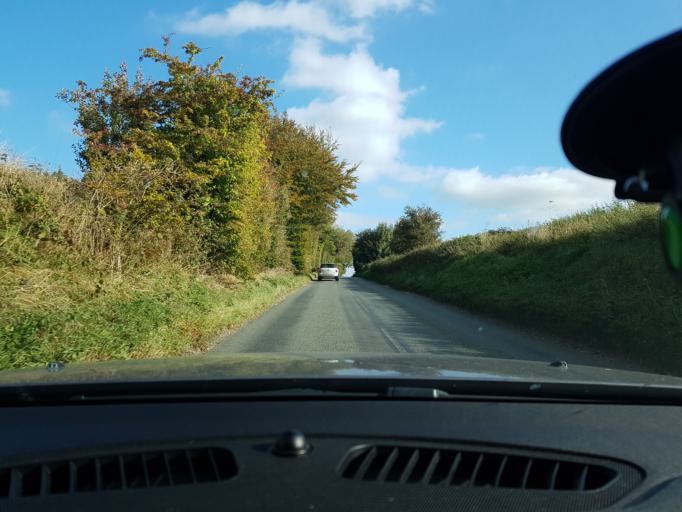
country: GB
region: England
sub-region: Wiltshire
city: Aldbourne
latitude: 51.5091
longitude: -1.6213
